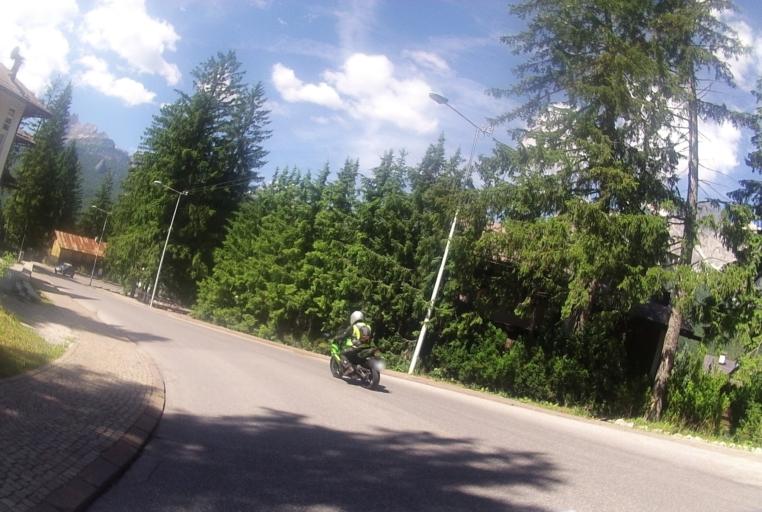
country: IT
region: Veneto
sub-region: Provincia di Belluno
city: Cortina d'Ampezzo
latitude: 46.5410
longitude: 12.1397
